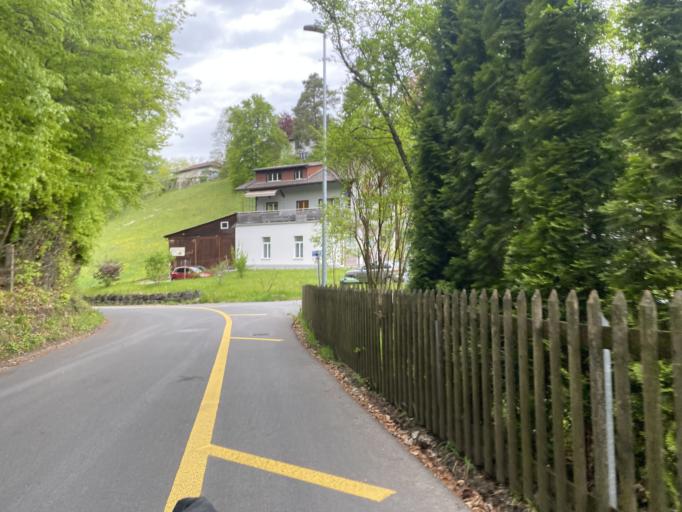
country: CH
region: Bern
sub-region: Thun District
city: Hilterfingen
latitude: 46.7487
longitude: 7.6442
